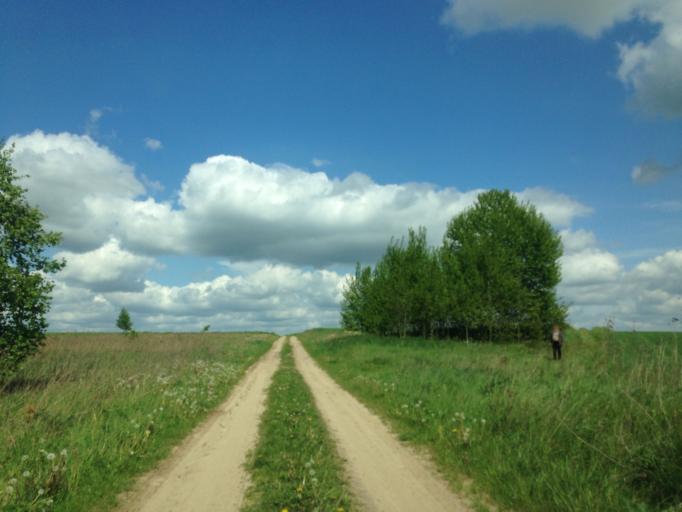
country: PL
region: Warmian-Masurian Voivodeship
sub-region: Powiat ostrodzki
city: Dabrowno
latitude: 53.3924
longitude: 20.1369
